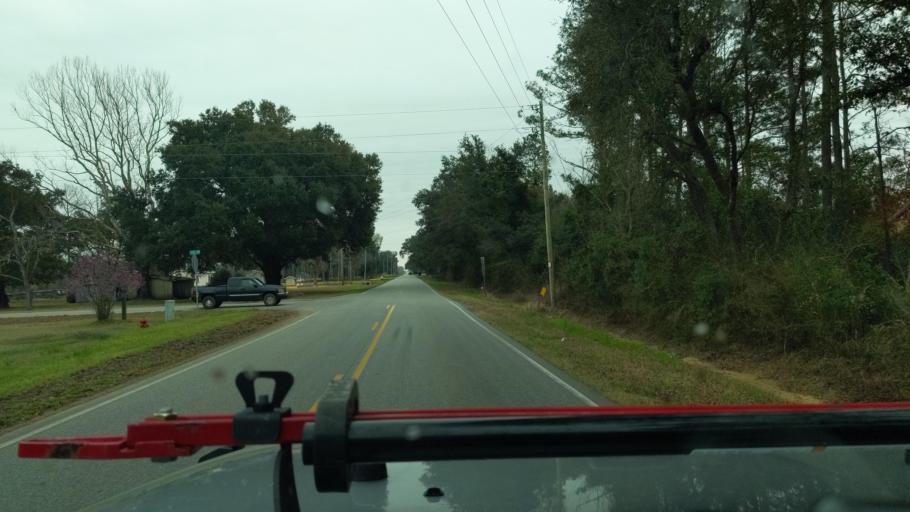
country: US
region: Alabama
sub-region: Baldwin County
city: Foley
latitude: 30.4579
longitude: -87.7683
